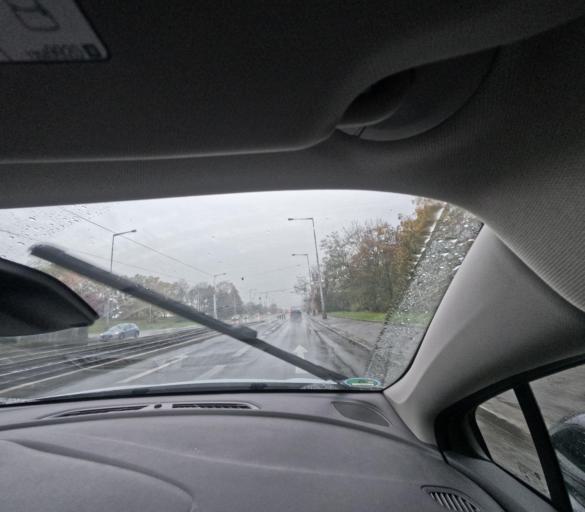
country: CZ
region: Central Bohemia
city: Horomerice
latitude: 50.0805
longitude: 14.3487
